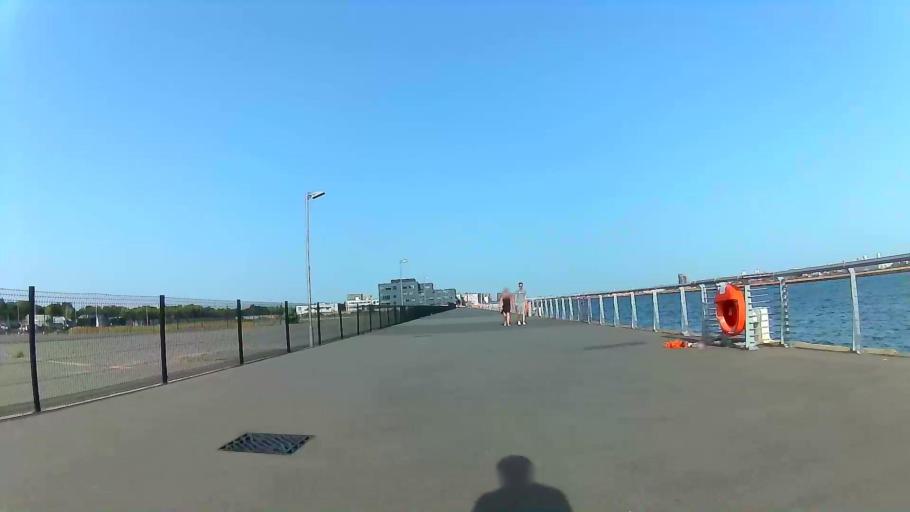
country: GB
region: England
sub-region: Greater London
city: Woolwich
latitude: 51.5073
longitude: 0.0549
